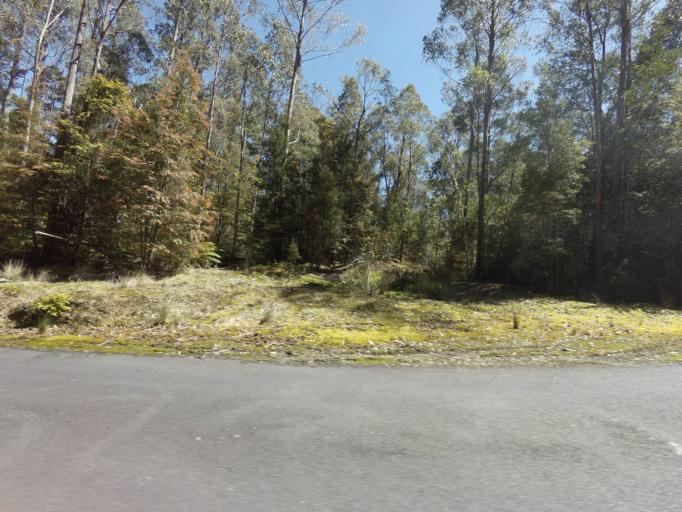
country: AU
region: Tasmania
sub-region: Huon Valley
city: Geeveston
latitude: -42.8170
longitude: 146.3452
